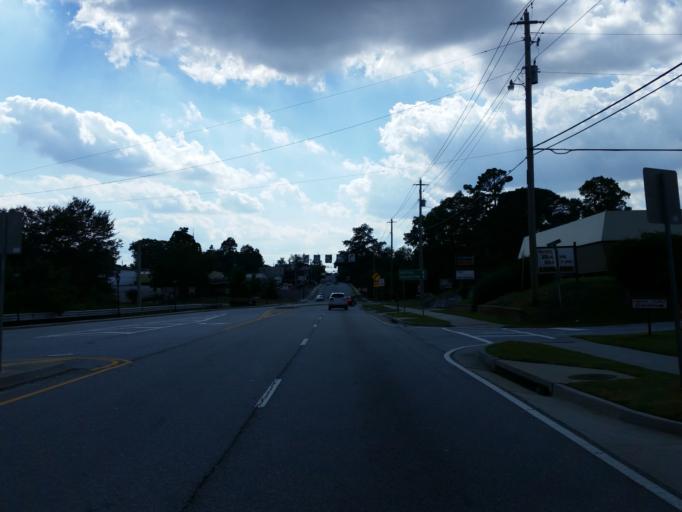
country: US
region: Georgia
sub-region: Gwinnett County
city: Lawrenceville
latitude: 33.9568
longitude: -83.9806
